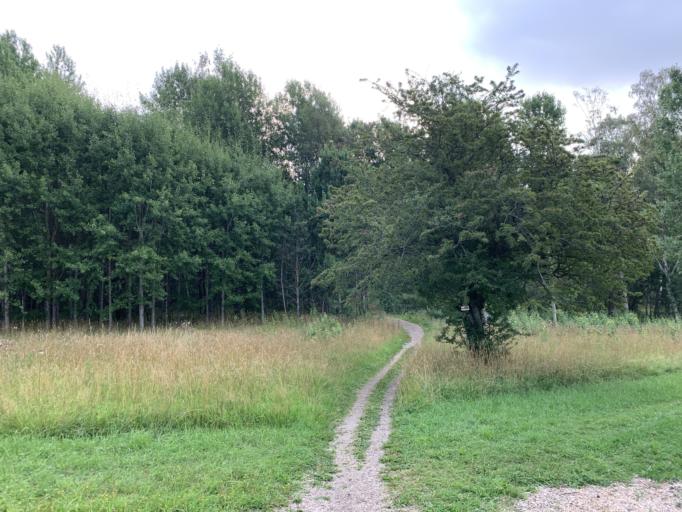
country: SE
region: Stockholm
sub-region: Solna Kommun
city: Rasunda
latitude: 59.3952
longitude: 17.9746
